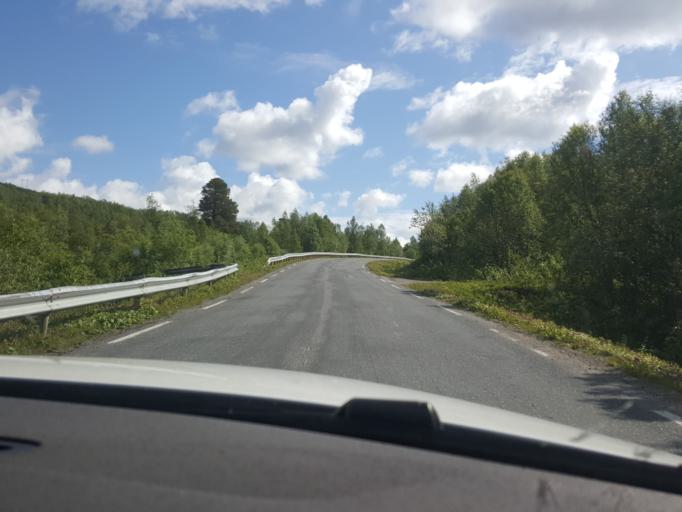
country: NO
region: Nordland
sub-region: Saltdal
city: Rognan
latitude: 67.0401
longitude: 15.0951
